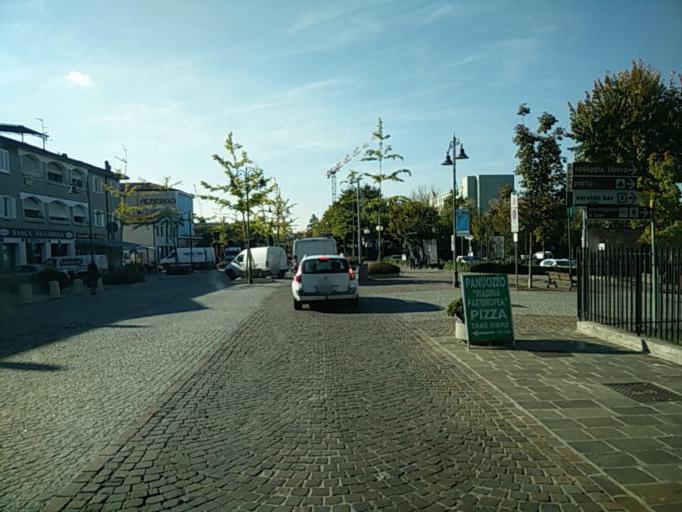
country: IT
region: Lombardy
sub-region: Provincia di Brescia
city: Desenzano del Garda
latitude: 45.4608
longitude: 10.5679
